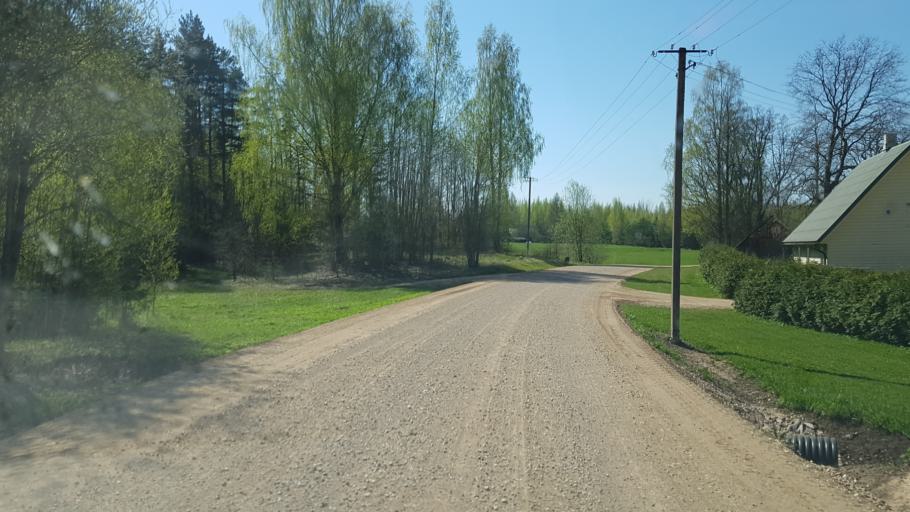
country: EE
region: Polvamaa
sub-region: Polva linn
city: Polva
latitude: 58.1097
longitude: 27.2394
